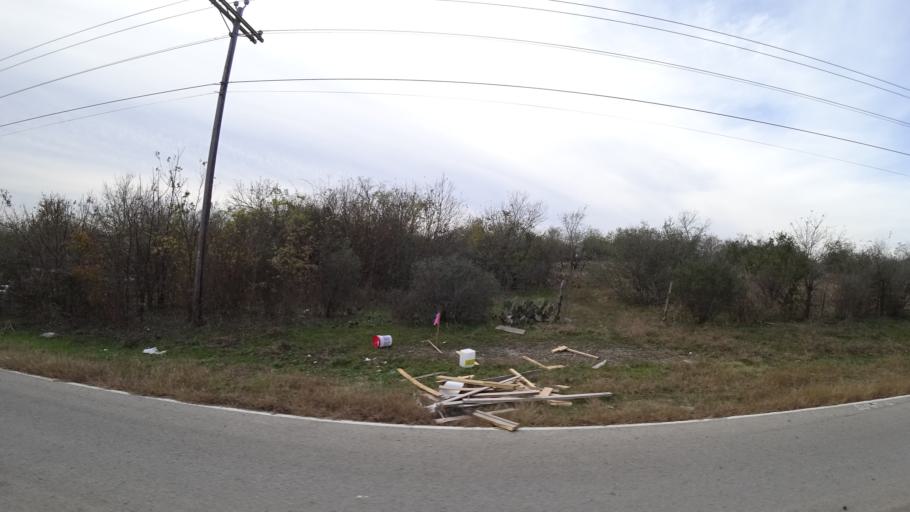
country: US
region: Texas
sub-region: Travis County
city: Onion Creek
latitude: 30.1571
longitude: -97.7249
